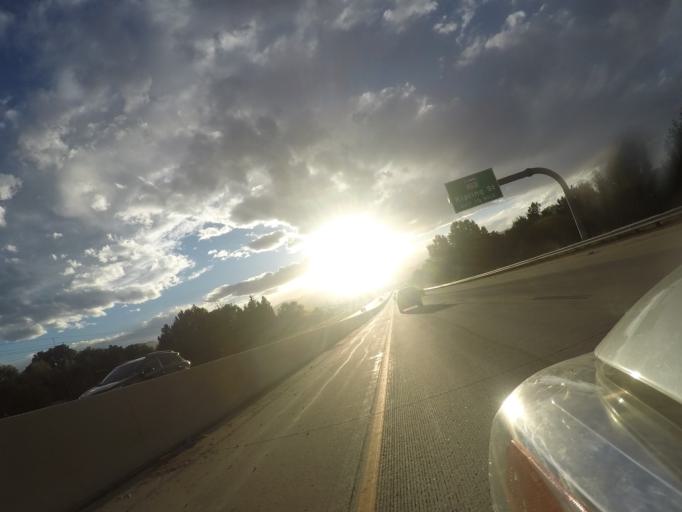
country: US
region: Colorado
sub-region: Jefferson County
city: Lakewood
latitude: 39.6536
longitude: -105.0973
